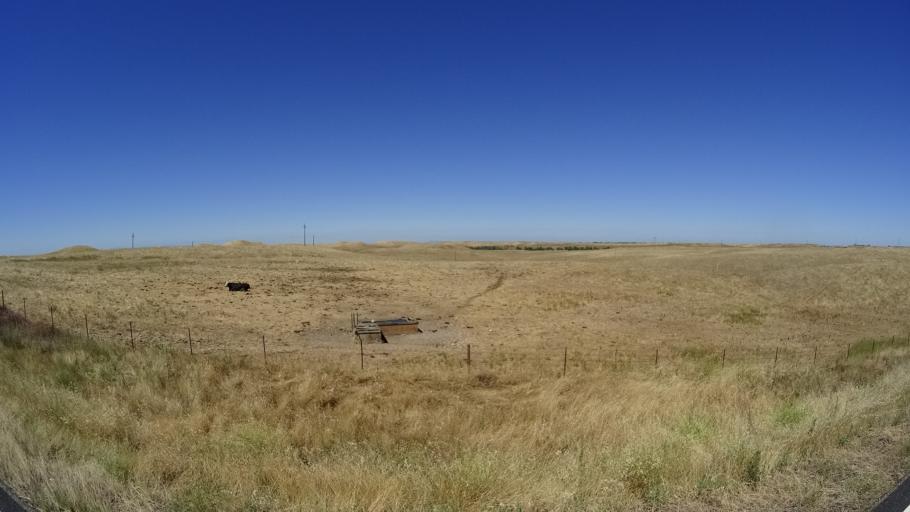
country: US
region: California
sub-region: Calaveras County
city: Rancho Calaveras
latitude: 38.0438
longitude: -120.8592
